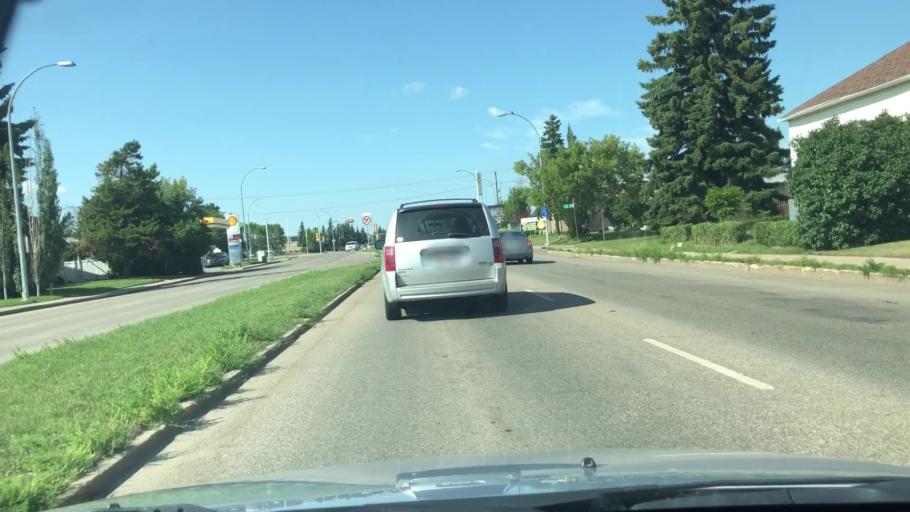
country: CA
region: Alberta
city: Edmonton
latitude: 53.5977
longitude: -113.4429
